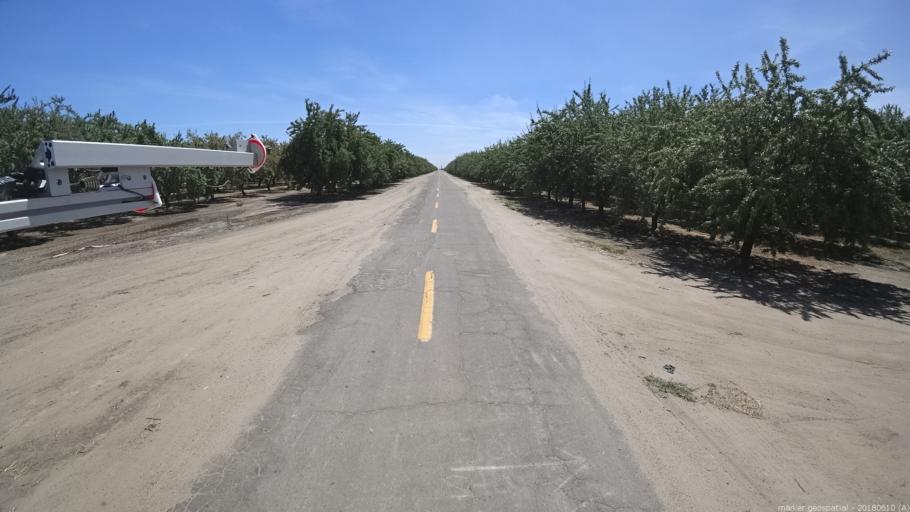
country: US
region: California
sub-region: Madera County
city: Chowchilla
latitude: 37.0398
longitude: -120.3964
